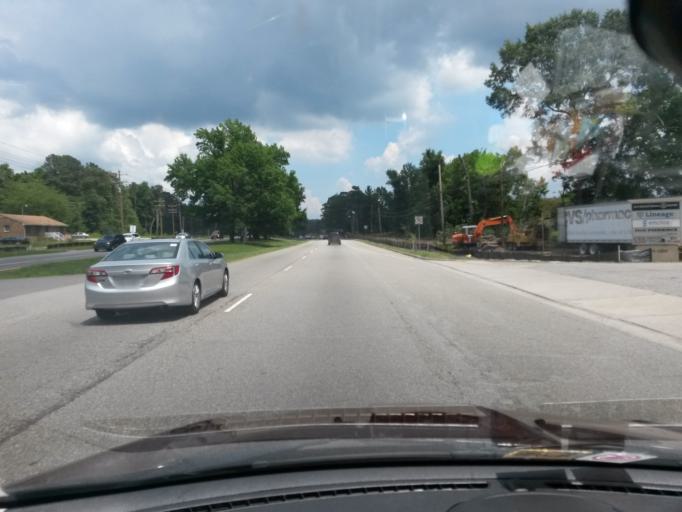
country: US
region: Virginia
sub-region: Chesterfield County
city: Chester
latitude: 37.3500
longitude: -77.3808
